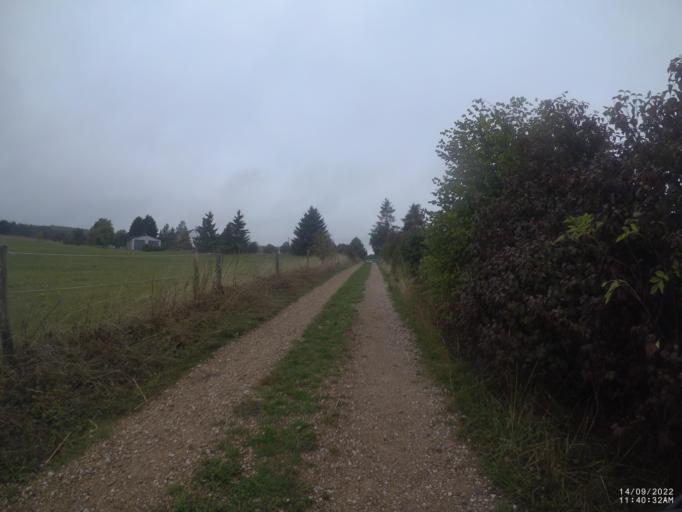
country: DE
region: Rheinland-Pfalz
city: Berndorf
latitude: 50.3225
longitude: 6.7273
